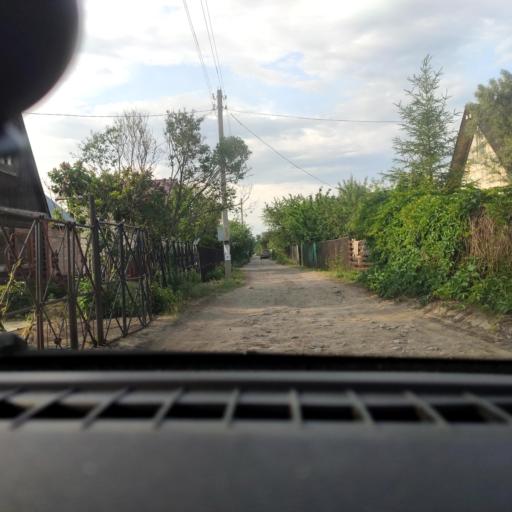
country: RU
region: Samara
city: Tol'yatti
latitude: 53.5928
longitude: 49.3203
